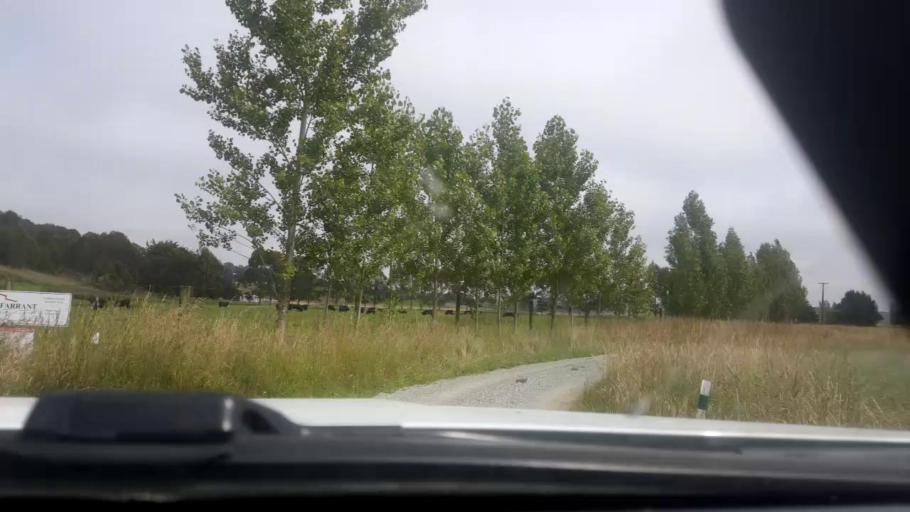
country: NZ
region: Canterbury
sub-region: Timaru District
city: Pleasant Point
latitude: -44.3252
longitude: 171.1944
